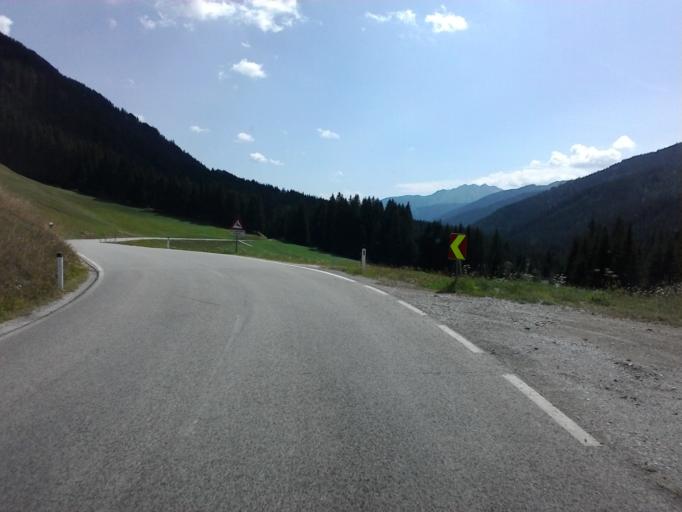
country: AT
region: Tyrol
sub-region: Politischer Bezirk Lienz
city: Obertilliach
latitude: 46.7142
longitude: 12.5703
